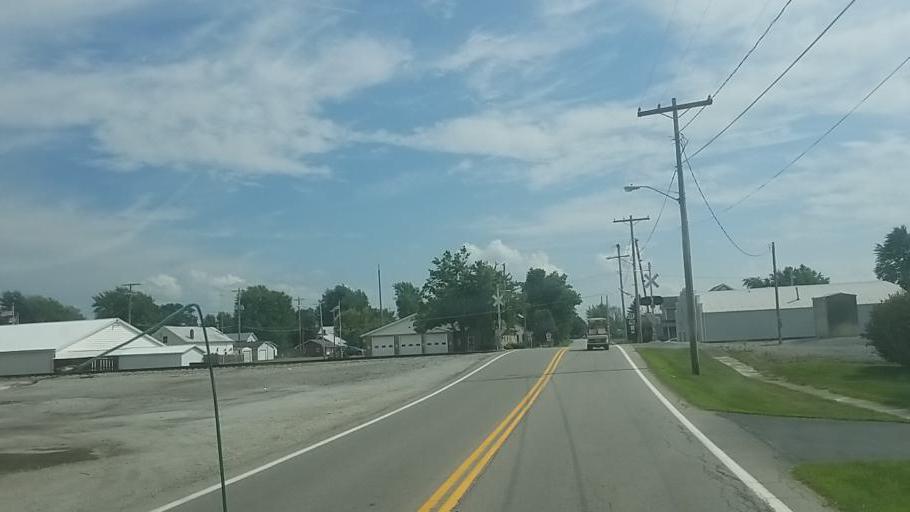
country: US
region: Ohio
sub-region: Hardin County
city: Forest
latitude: 40.8026
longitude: -83.5147
